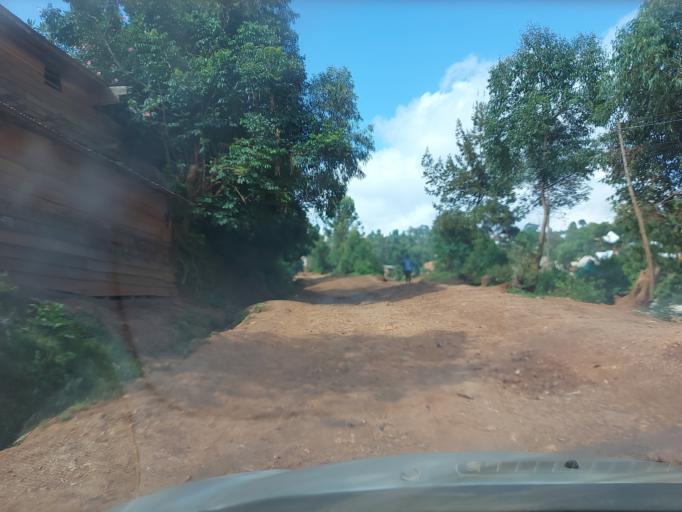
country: CD
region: South Kivu
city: Bukavu
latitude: -2.5113
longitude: 28.8398
